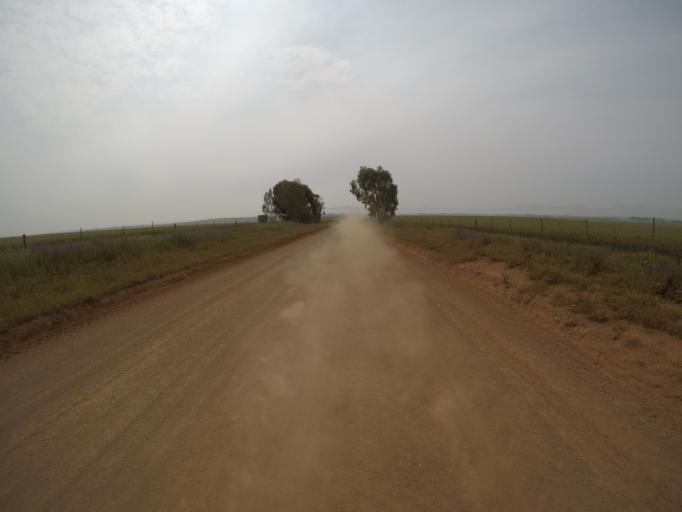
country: ZA
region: Western Cape
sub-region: City of Cape Town
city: Kraaifontein
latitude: -33.7187
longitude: 18.6789
